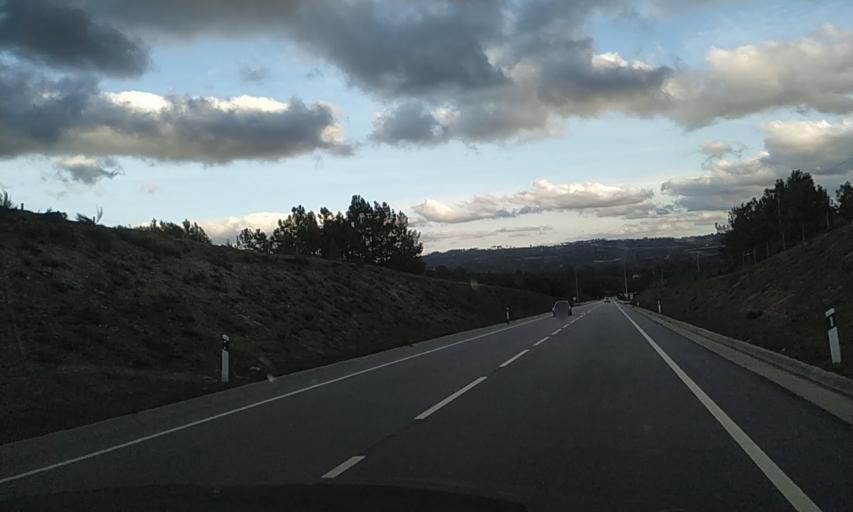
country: PT
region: Vila Real
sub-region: Murca
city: Murca
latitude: 41.3685
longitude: -7.5013
